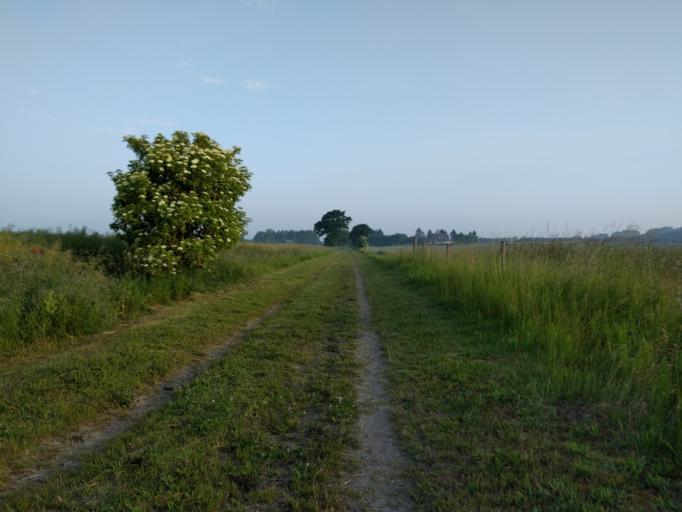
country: DK
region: South Denmark
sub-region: Kerteminde Kommune
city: Munkebo
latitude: 55.4351
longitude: 10.5370
